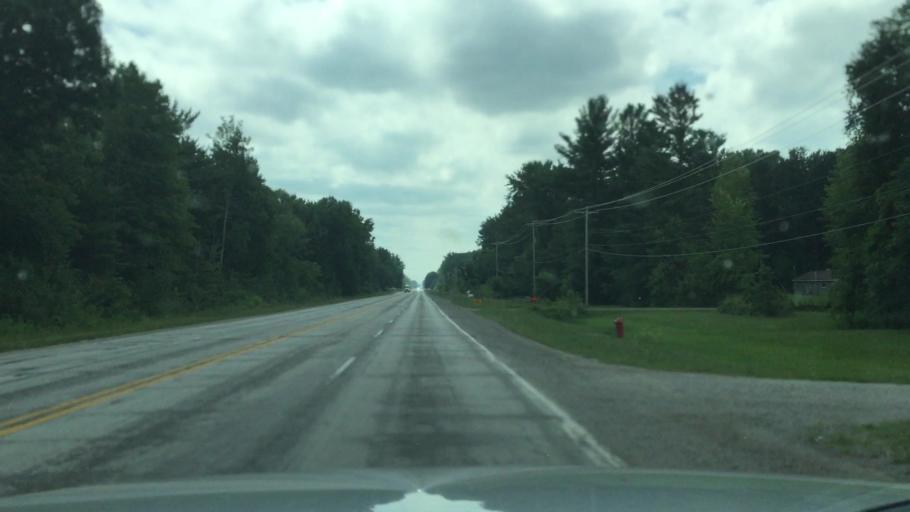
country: US
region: Michigan
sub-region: Saginaw County
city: Birch Run
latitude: 43.2915
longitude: -83.8006
